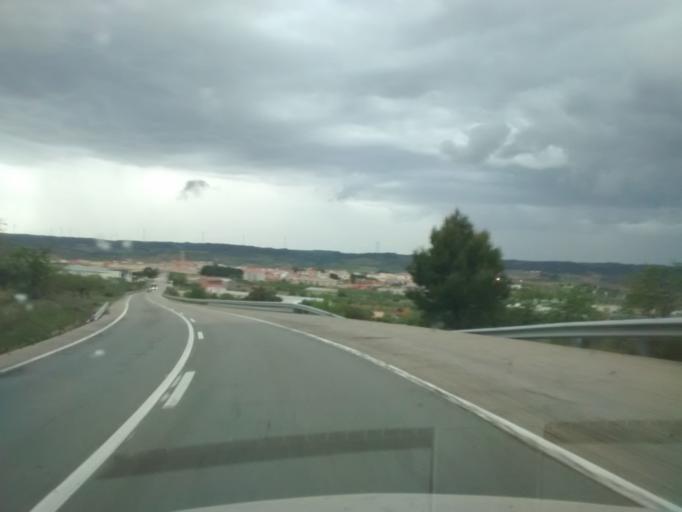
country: ES
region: Catalonia
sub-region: Provincia de Tarragona
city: Gandesa
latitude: 41.0467
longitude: 0.4519
